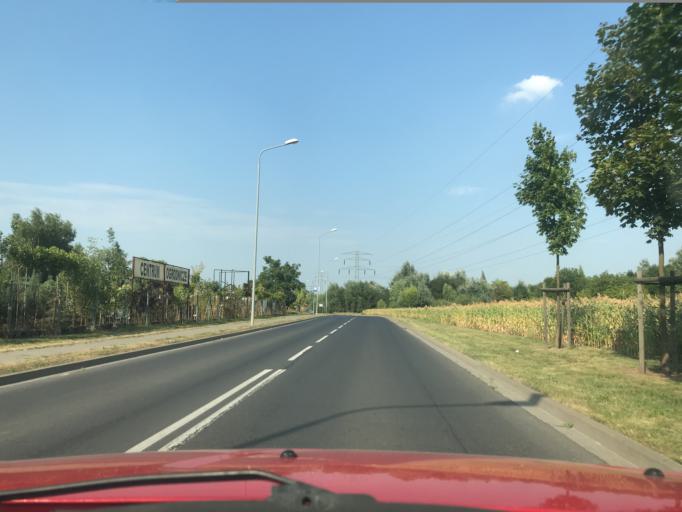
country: PL
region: Greater Poland Voivodeship
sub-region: Powiat poznanski
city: Plewiska
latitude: 52.3632
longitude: 16.8520
